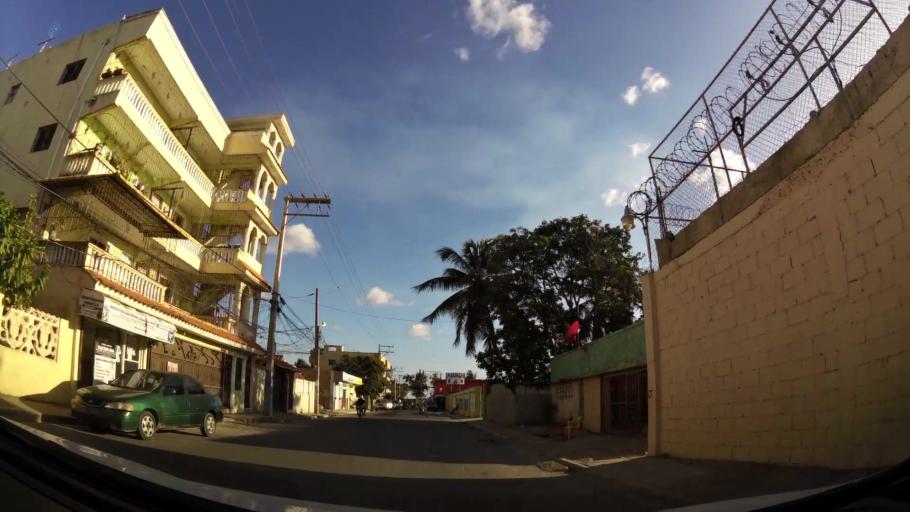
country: DO
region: Santo Domingo
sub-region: Santo Domingo
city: Santo Domingo Este
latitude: 18.4683
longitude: -69.7946
